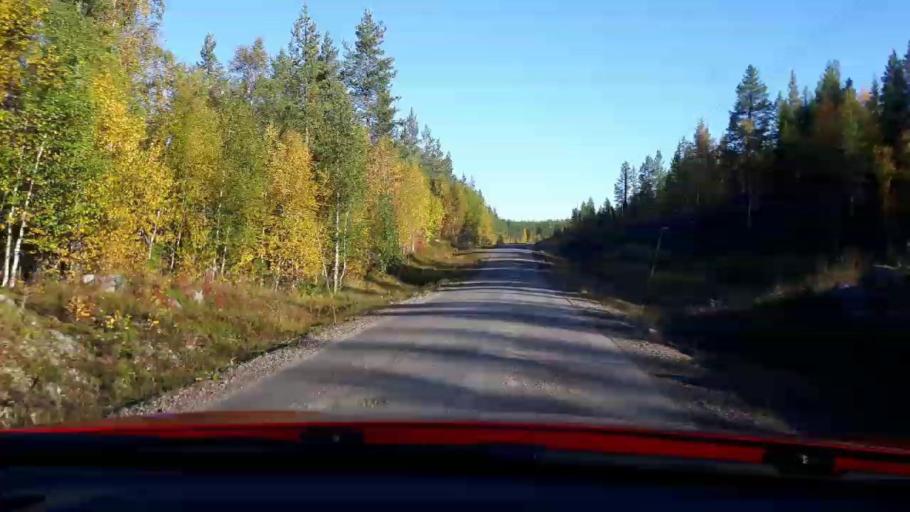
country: SE
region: Jaemtland
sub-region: Stroemsunds Kommun
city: Stroemsund
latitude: 64.3759
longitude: 15.1507
